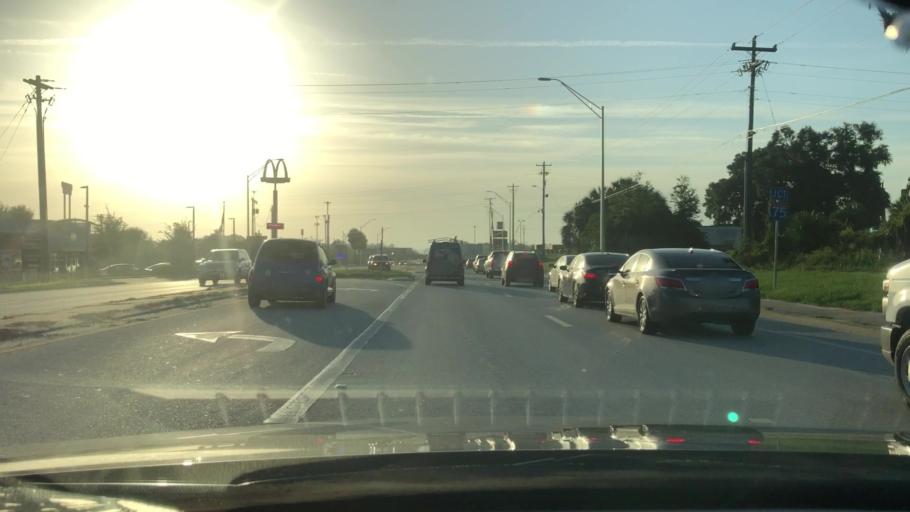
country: US
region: Florida
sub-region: Marion County
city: Belleview
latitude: 29.0255
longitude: -82.1615
